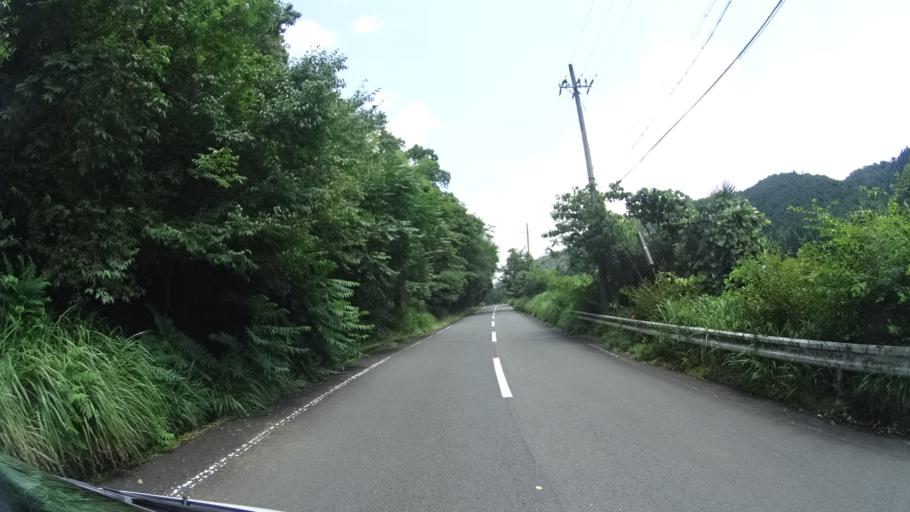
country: JP
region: Kyoto
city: Ayabe
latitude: 35.1918
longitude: 135.2455
